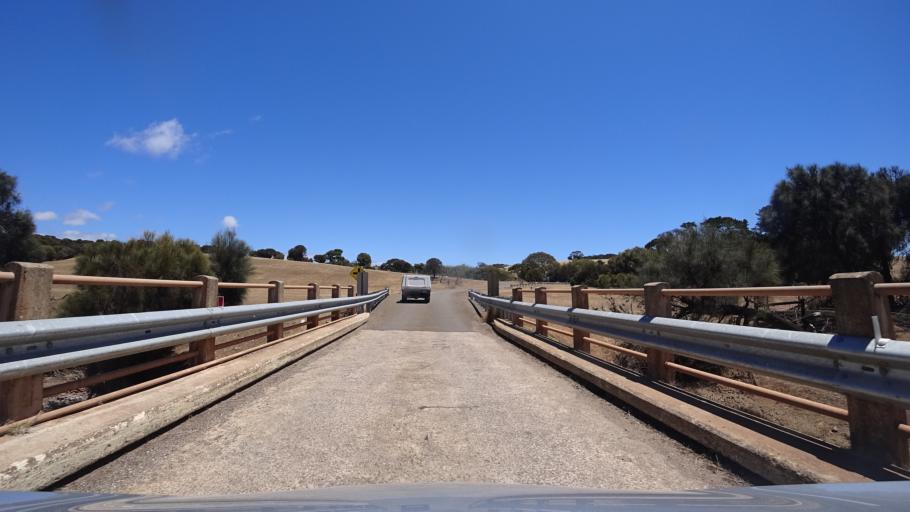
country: AU
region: South Australia
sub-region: Kangaroo Island
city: Kingscote
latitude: -35.6291
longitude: 137.2052
